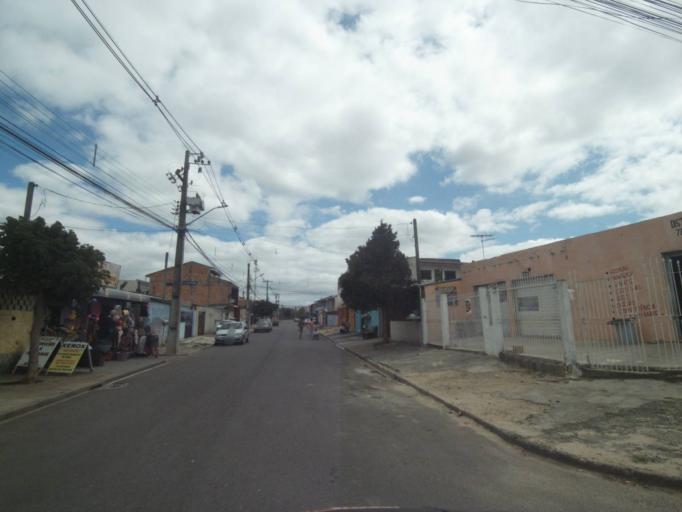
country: BR
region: Parana
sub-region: Sao Jose Dos Pinhais
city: Sao Jose dos Pinhais
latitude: -25.5555
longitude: -49.2657
